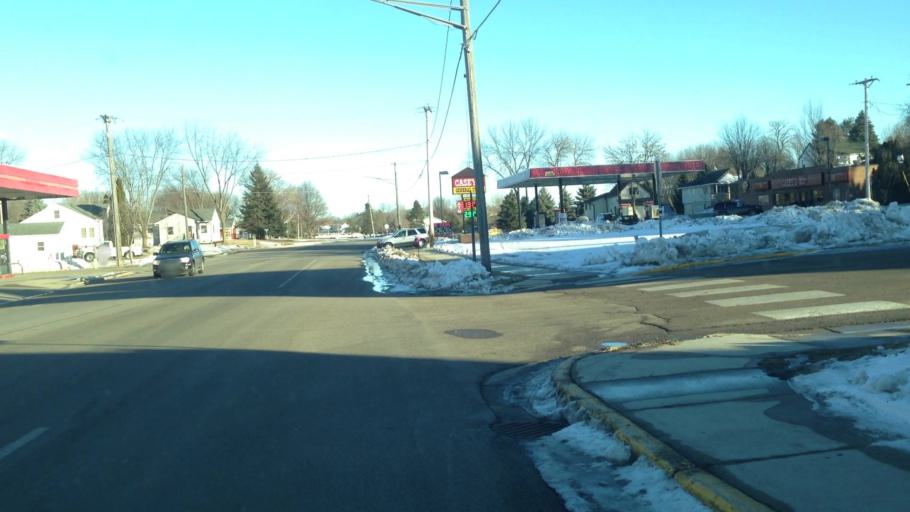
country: US
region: Minnesota
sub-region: Rice County
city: Lonsdale
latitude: 44.4805
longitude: -93.4259
